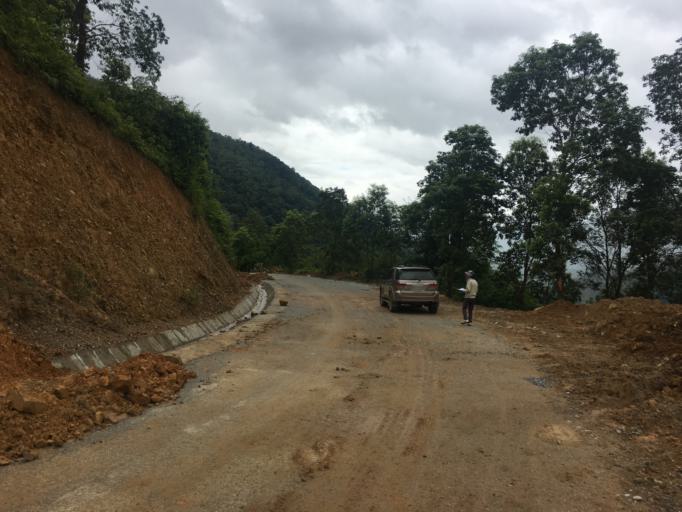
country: VN
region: Ha Giang
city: Thi Tran Tam Son
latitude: 22.9946
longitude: 105.0683
